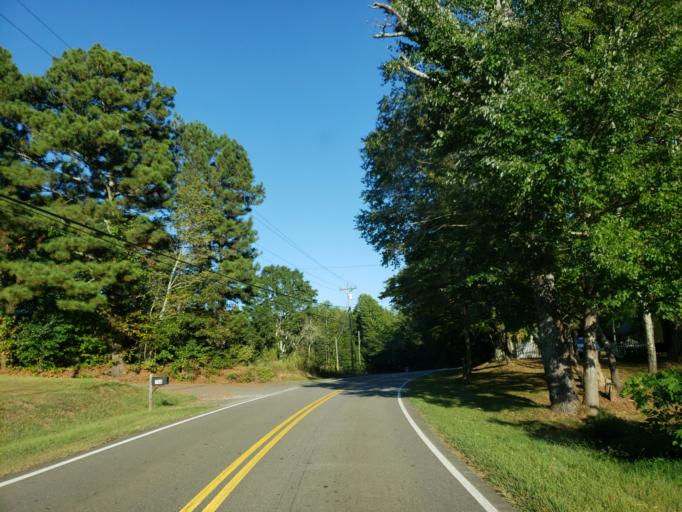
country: US
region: Georgia
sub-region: Pickens County
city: Nelson
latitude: 34.4008
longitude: -84.3970
